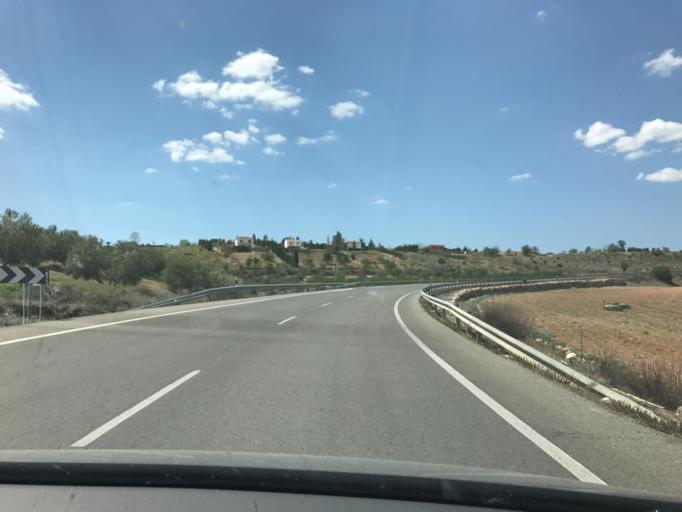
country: ES
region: Andalusia
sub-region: Provincia de Jaen
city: Frailes
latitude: 37.4460
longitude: -3.8651
